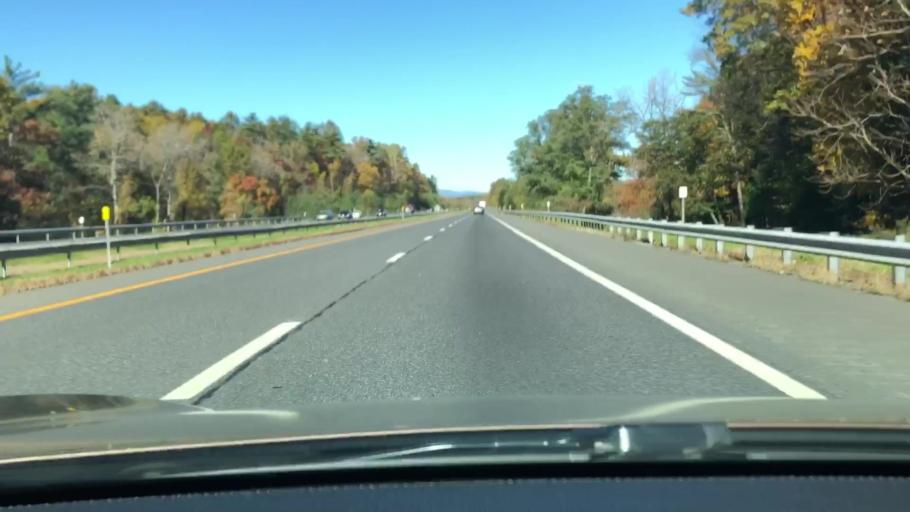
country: US
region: New York
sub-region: Ulster County
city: Rosendale Village
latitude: 41.8726
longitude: -74.0581
